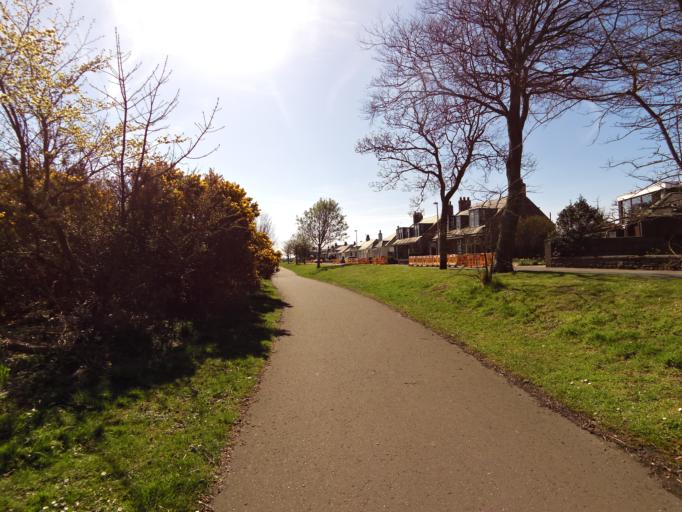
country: GB
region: Scotland
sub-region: Angus
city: Montrose
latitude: 56.7178
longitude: -2.4577
